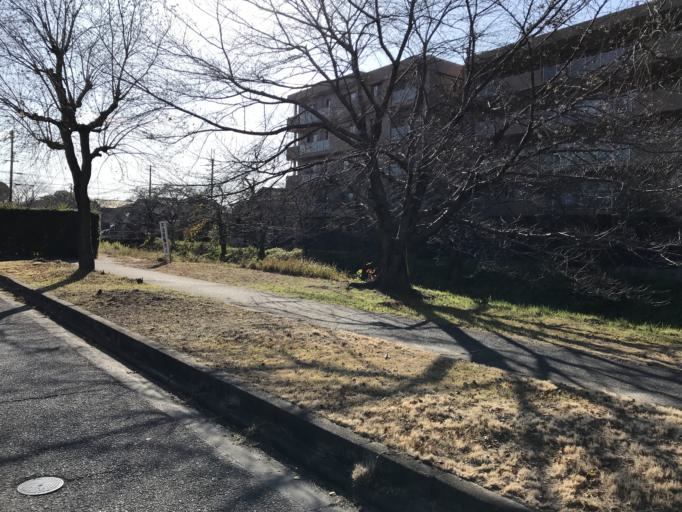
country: JP
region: Kyoto
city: Tanabe
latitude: 34.8205
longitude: 135.7765
